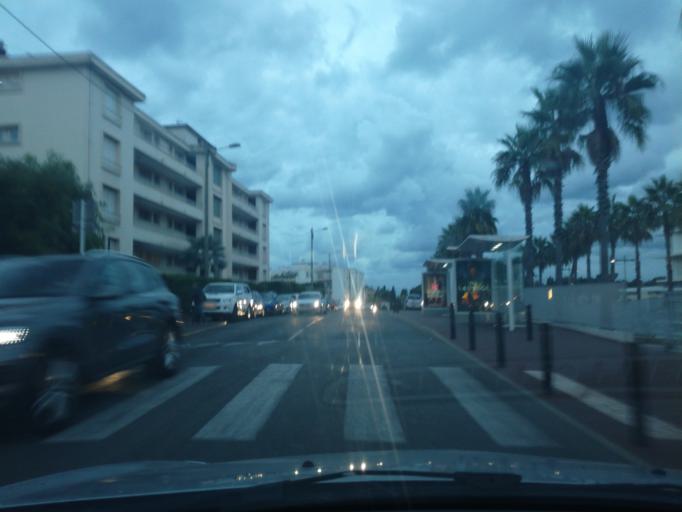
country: FR
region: Provence-Alpes-Cote d'Azur
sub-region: Departement des Alpes-Maritimes
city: Cannes
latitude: 43.5637
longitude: 7.0057
